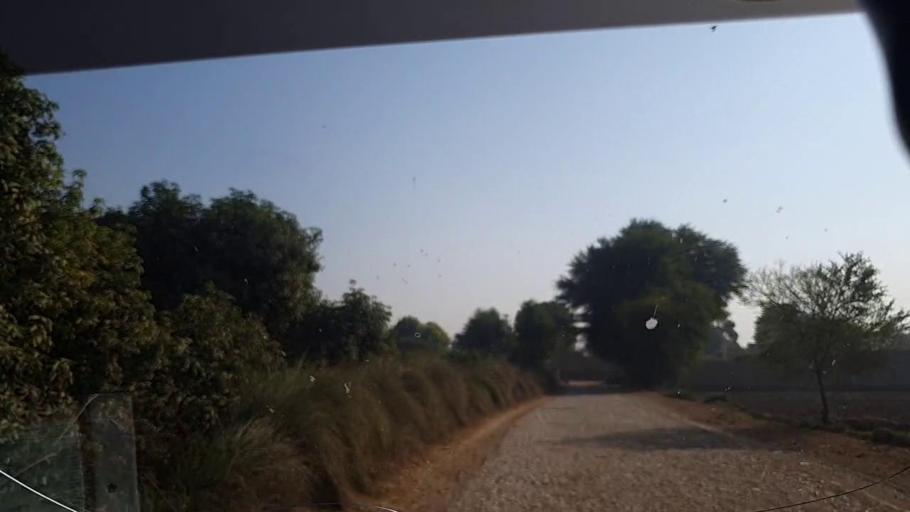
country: PK
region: Sindh
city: Hingorja
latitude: 27.2135
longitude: 68.2645
